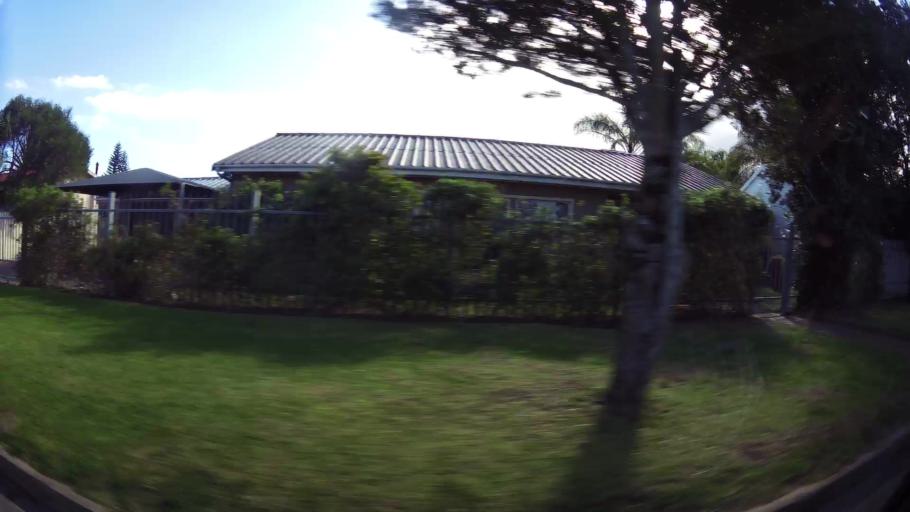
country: ZA
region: Western Cape
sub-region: Eden District Municipality
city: George
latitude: -33.9610
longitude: 22.4888
